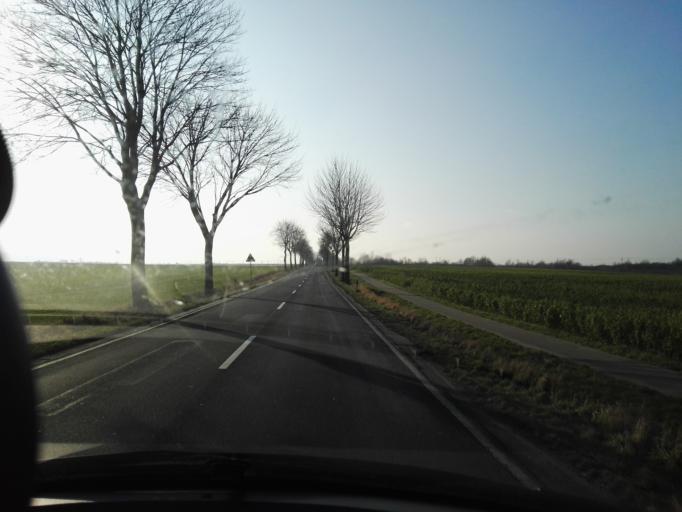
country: DE
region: Lower Saxony
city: Sarstedt
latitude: 52.2115
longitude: 9.8307
